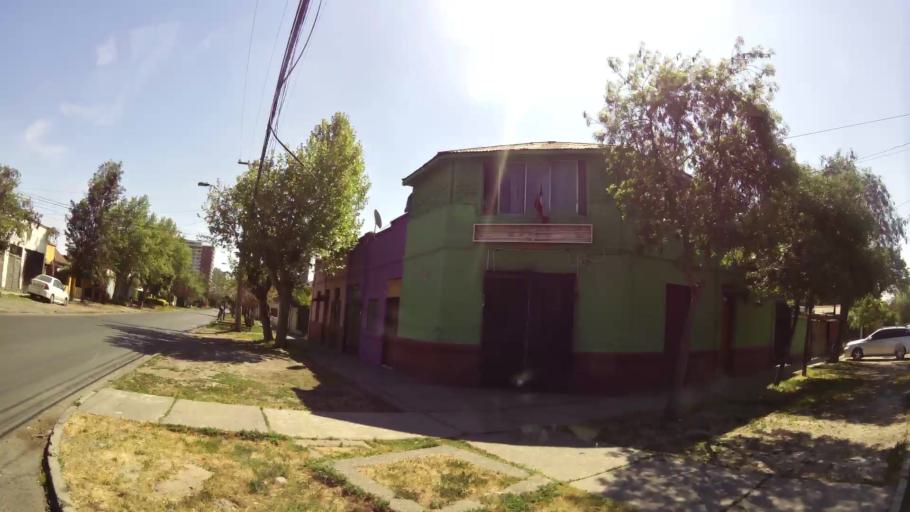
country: CL
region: Santiago Metropolitan
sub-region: Provincia de Santiago
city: Santiago
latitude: -33.5088
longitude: -70.6495
